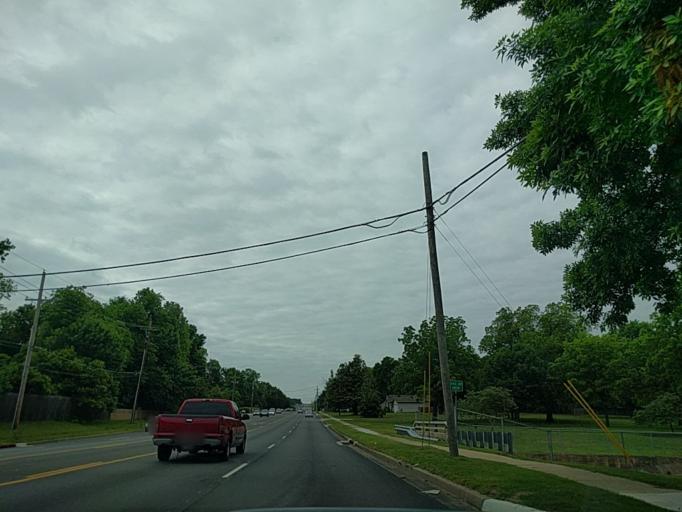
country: US
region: Oklahoma
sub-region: Tulsa County
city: Jenks
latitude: 36.0859
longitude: -95.9045
